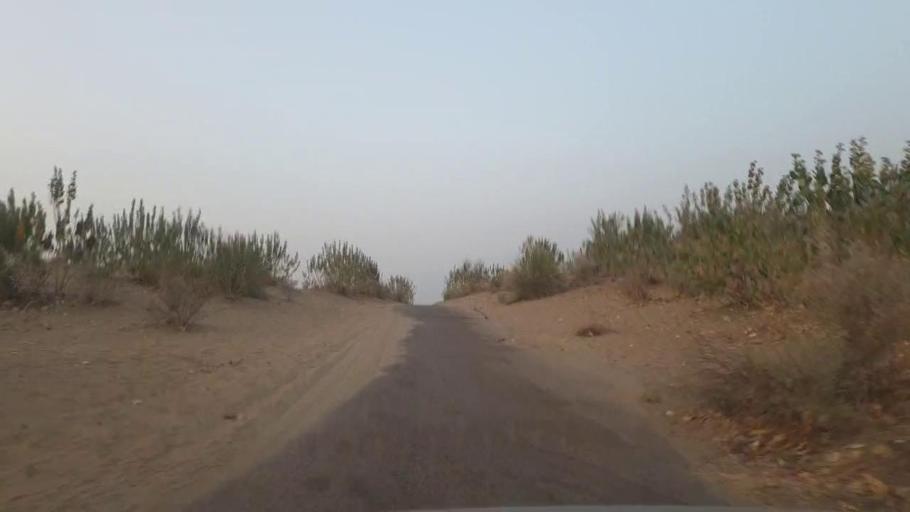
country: PK
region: Sindh
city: Umarkot
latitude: 25.3185
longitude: 70.0577
